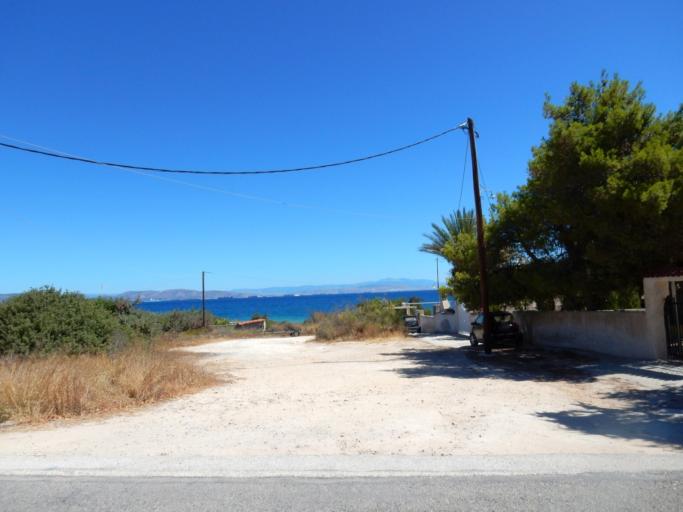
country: GR
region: Attica
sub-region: Nomos Piraios
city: Vathi
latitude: 37.7706
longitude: 23.5130
